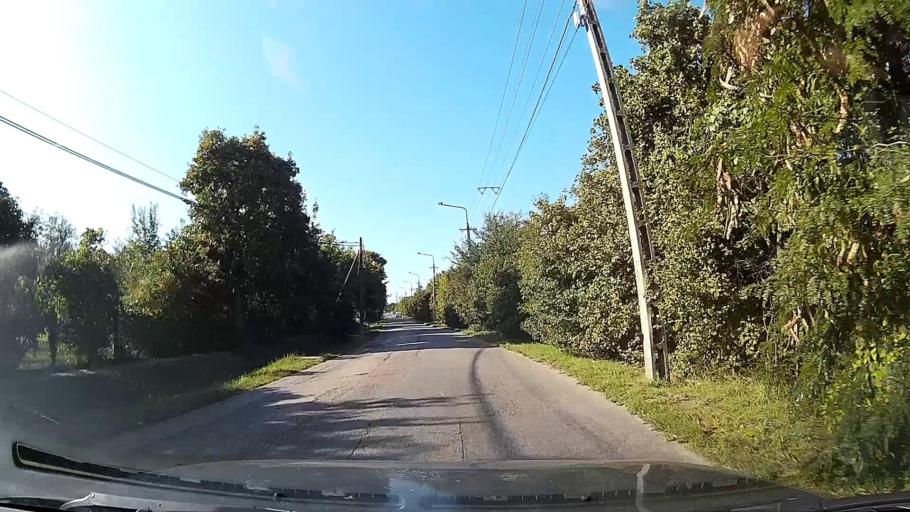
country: HU
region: Budapest
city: Budapest XXII. keruelet
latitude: 47.4212
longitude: 19.0061
